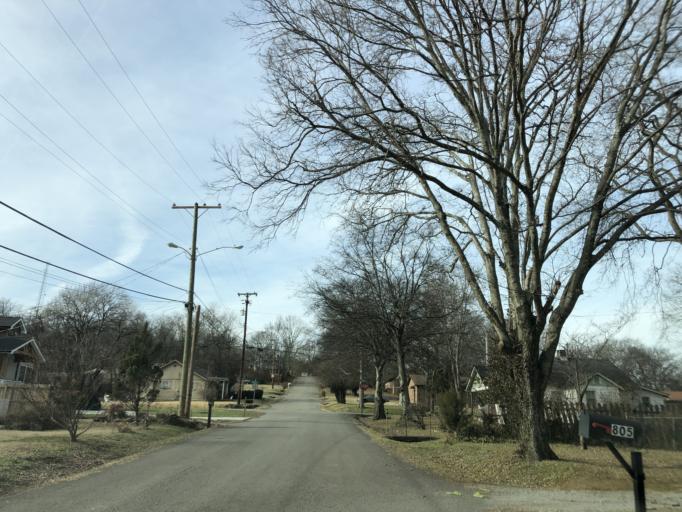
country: US
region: Tennessee
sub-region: Davidson County
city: Nashville
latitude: 36.2233
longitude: -86.7365
